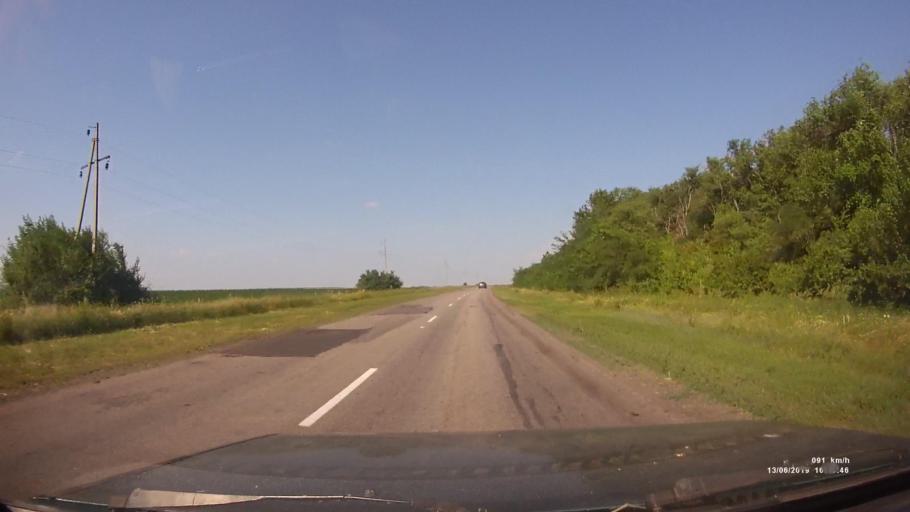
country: RU
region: Rostov
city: Kazanskaya
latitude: 49.8330
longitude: 41.2224
